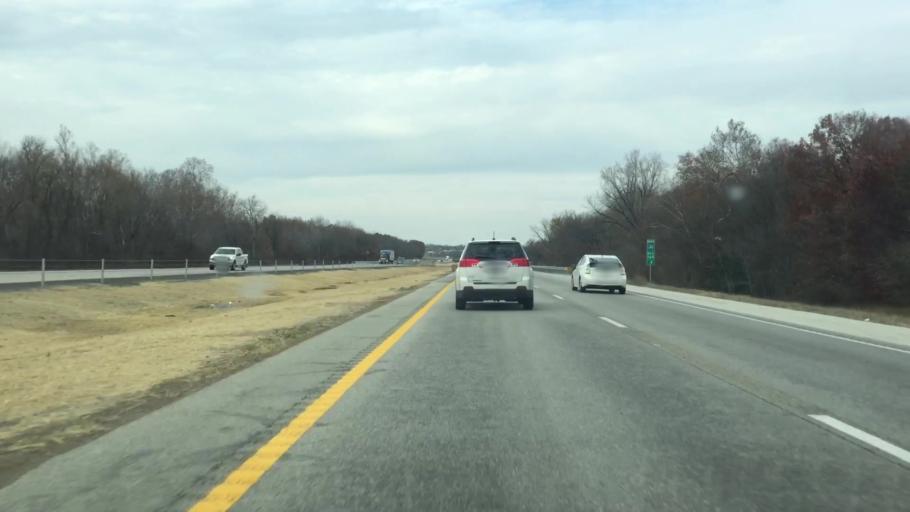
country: US
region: Missouri
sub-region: Cass County
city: Peculiar
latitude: 38.6882
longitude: -94.4256
